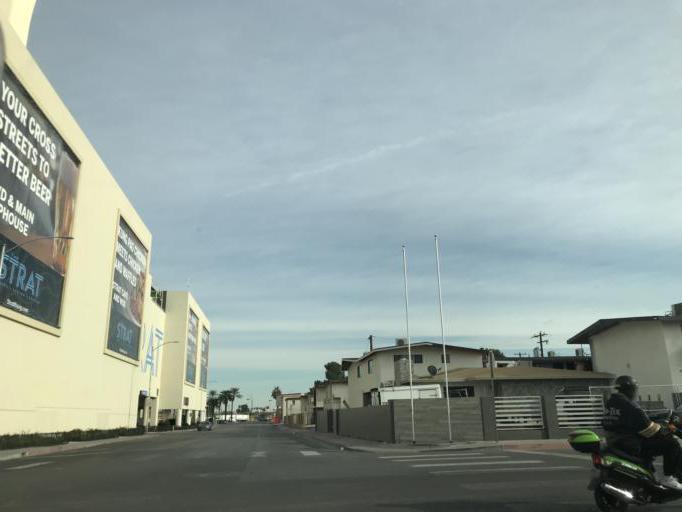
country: US
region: Nevada
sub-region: Clark County
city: Las Vegas
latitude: 36.1464
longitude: -115.1584
